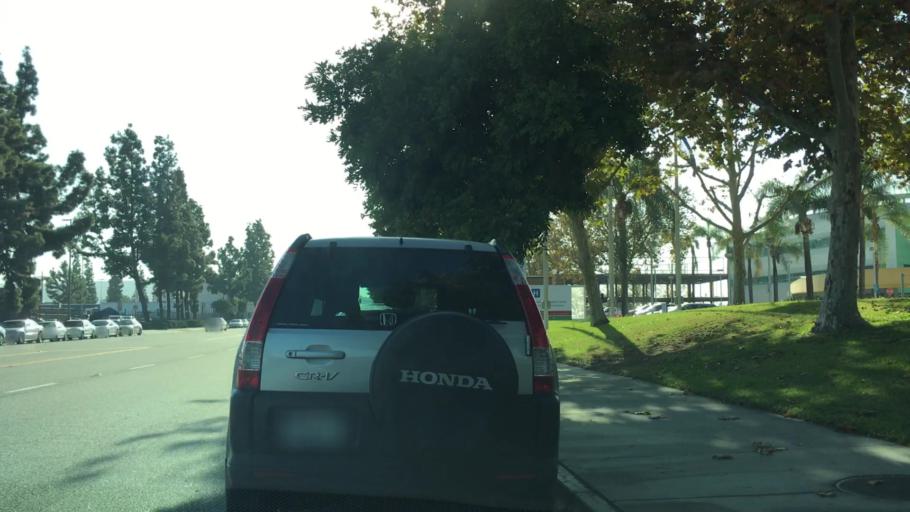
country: US
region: California
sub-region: Los Angeles County
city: West Puente Valley
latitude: 34.0651
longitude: -117.9844
